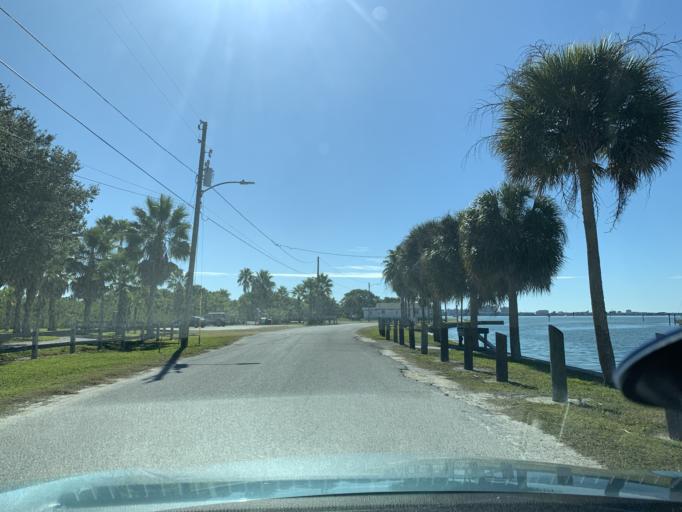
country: US
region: Florida
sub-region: Pinellas County
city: Gulfport
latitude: 27.7391
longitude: -82.6946
